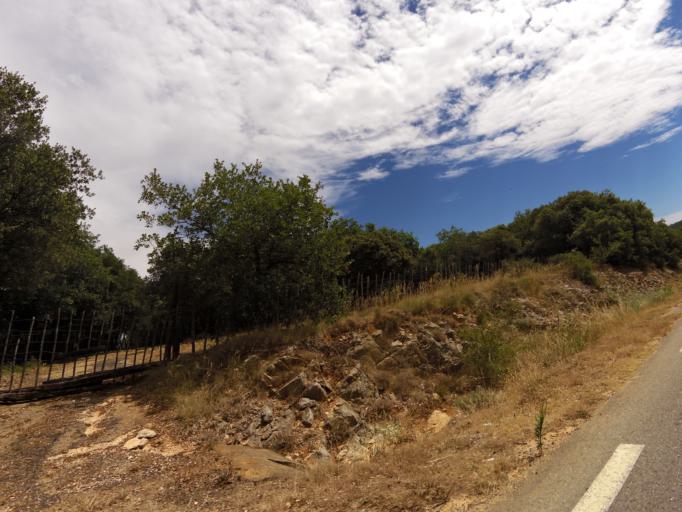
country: FR
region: Languedoc-Roussillon
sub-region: Departement du Gard
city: Quissac
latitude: 43.8729
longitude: 4.0148
